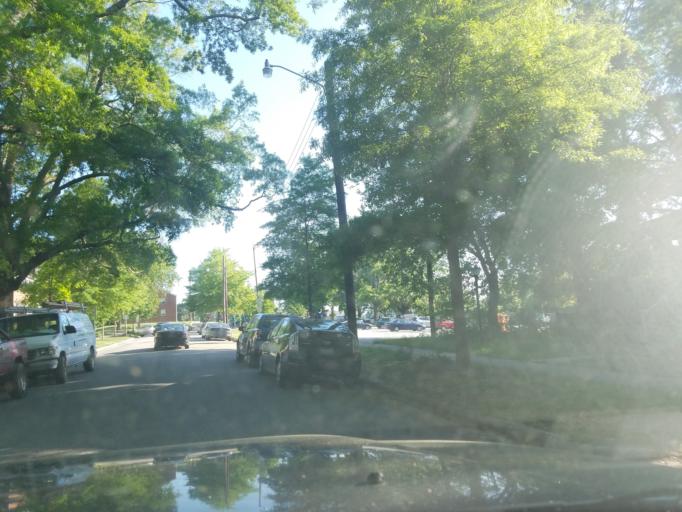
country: US
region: North Carolina
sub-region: Durham County
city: Durham
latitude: 36.0108
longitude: -78.9171
